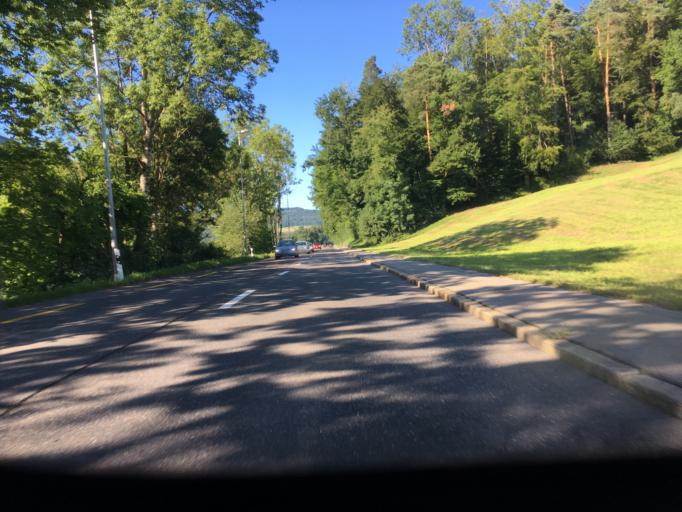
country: CH
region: Zug
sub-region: Zug
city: Baar
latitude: 47.1988
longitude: 8.5409
